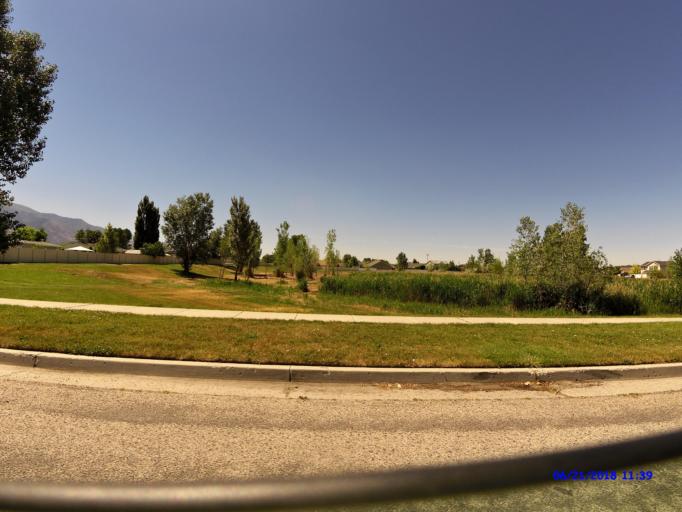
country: US
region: Utah
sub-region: Weber County
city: Harrisville
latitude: 41.2668
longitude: -111.9848
